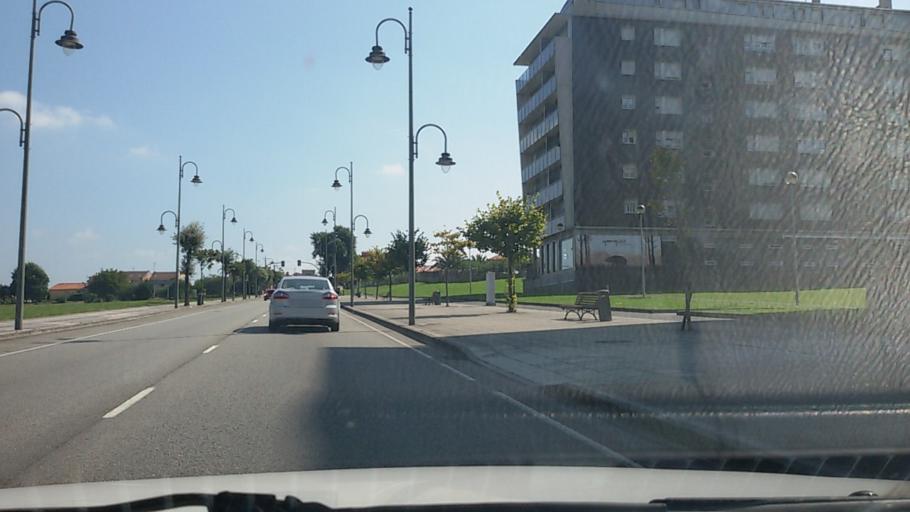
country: ES
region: Asturias
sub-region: Province of Asturias
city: Corvera de Asturias
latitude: 43.5362
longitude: -5.8939
